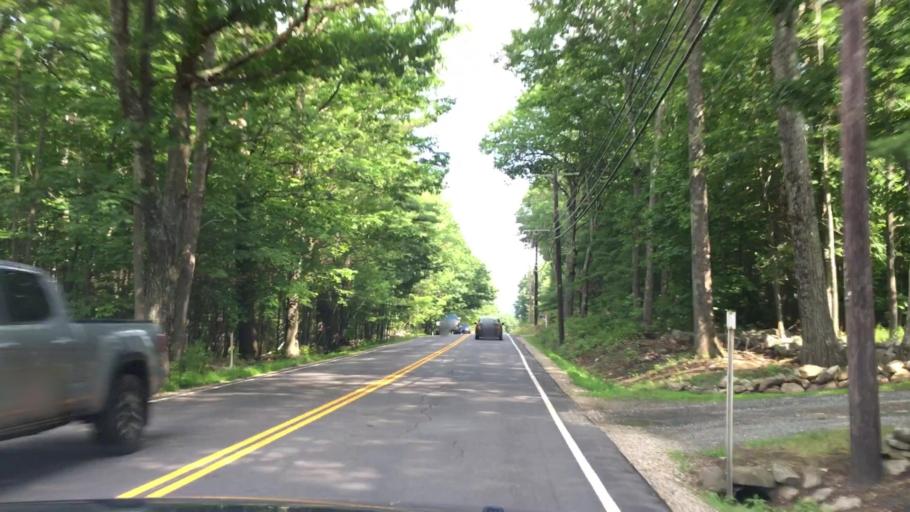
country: US
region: New Hampshire
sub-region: Belknap County
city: Gilford
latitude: 43.5679
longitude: -71.3414
